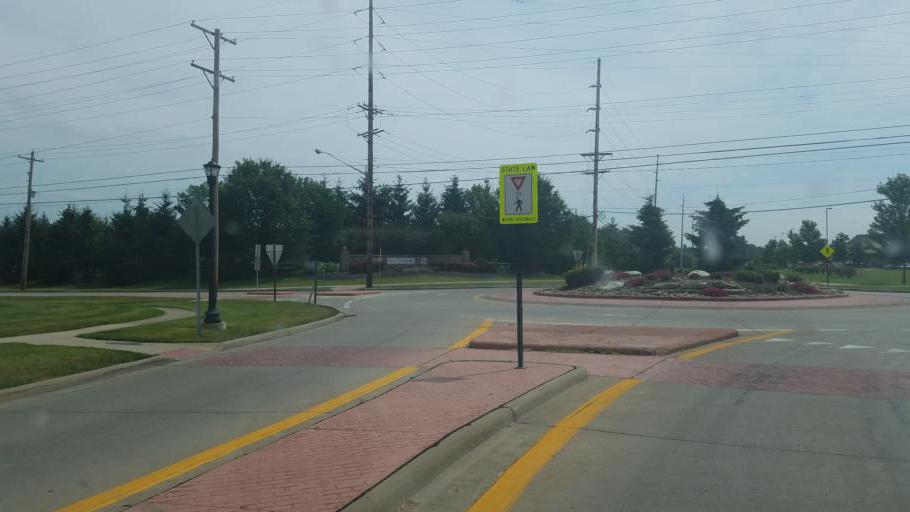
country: US
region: Ohio
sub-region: Summit County
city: Reminderville
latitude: 41.3416
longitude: -81.4194
